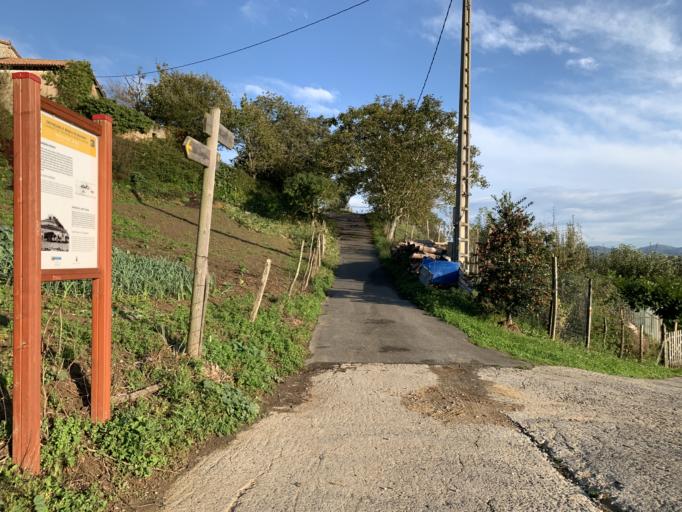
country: ES
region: Basque Country
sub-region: Provincia de Guipuzcoa
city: Zarautz
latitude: 43.2889
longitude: -2.1825
